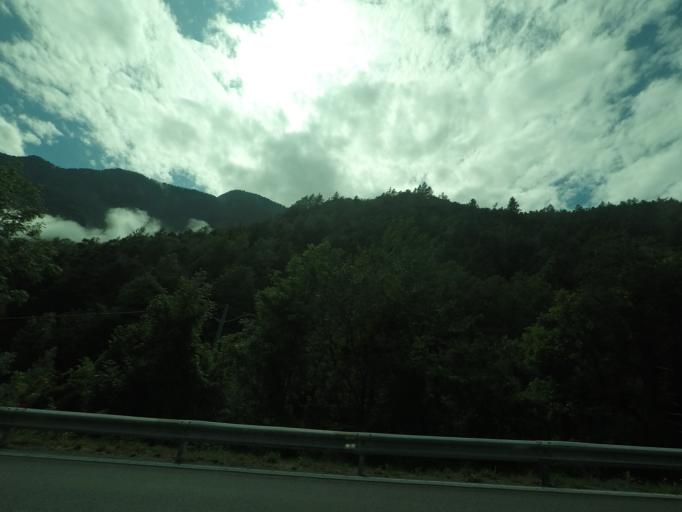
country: IT
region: Aosta Valley
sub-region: Valle d'Aosta
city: Antey-Saint-Andre
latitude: 45.7878
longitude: 7.5910
